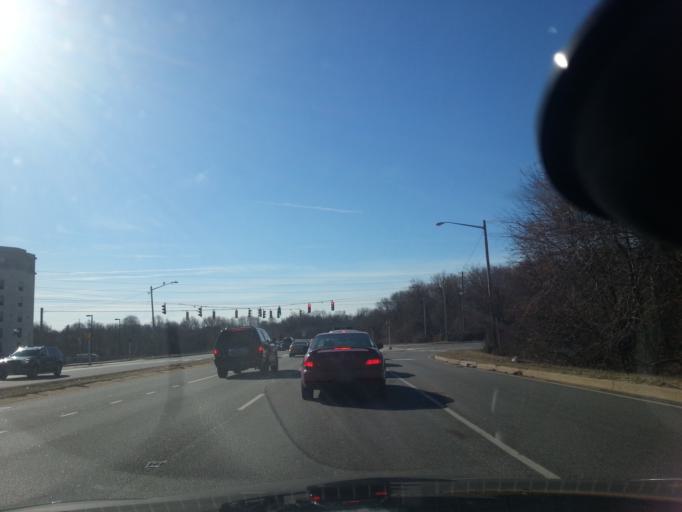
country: US
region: Delaware
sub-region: New Castle County
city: Bear
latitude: 39.6630
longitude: -75.6650
